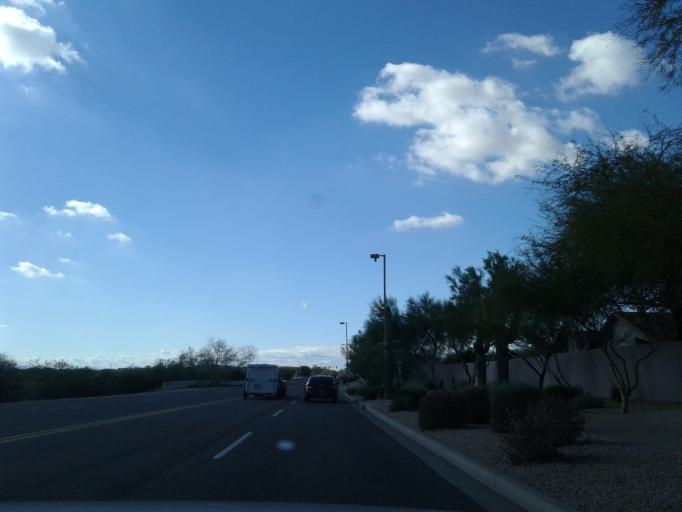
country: US
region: Arizona
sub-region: Maricopa County
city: Cave Creek
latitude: 33.6830
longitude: -111.9849
